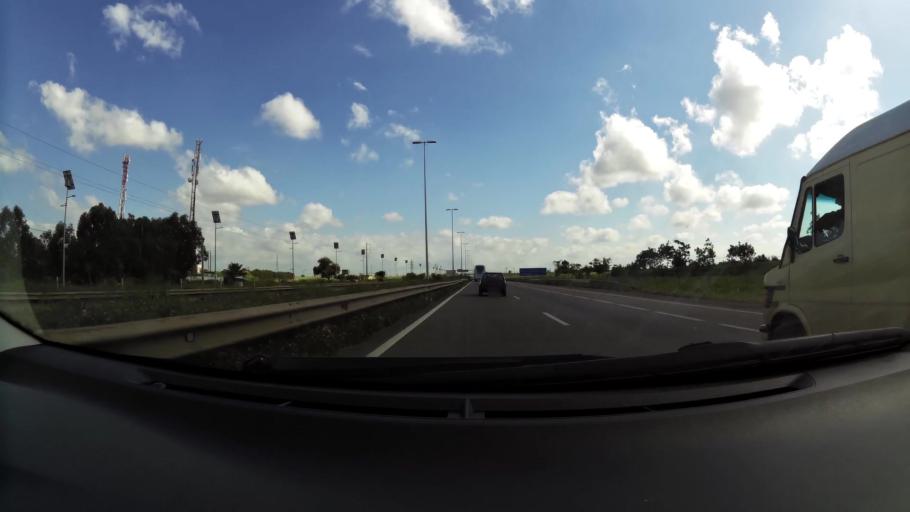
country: MA
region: Grand Casablanca
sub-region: Nouaceur
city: Bouskoura
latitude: 33.4313
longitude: -7.6280
